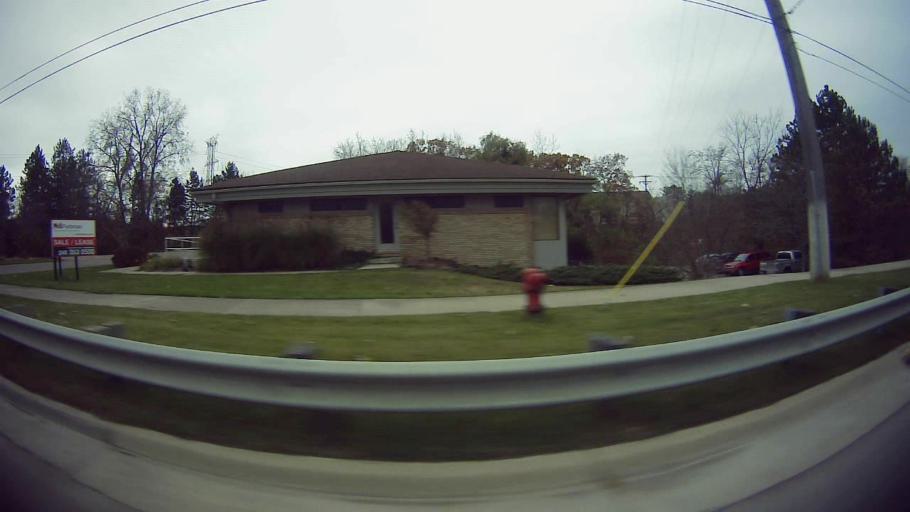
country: US
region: Michigan
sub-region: Oakland County
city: Clarkston
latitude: 42.7227
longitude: -83.4229
